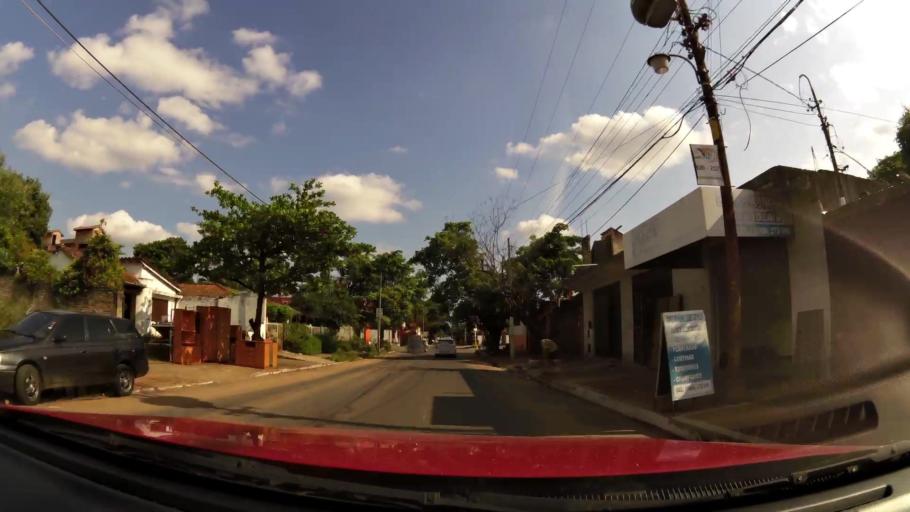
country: PY
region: Central
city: Fernando de la Mora
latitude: -25.3283
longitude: -57.5303
